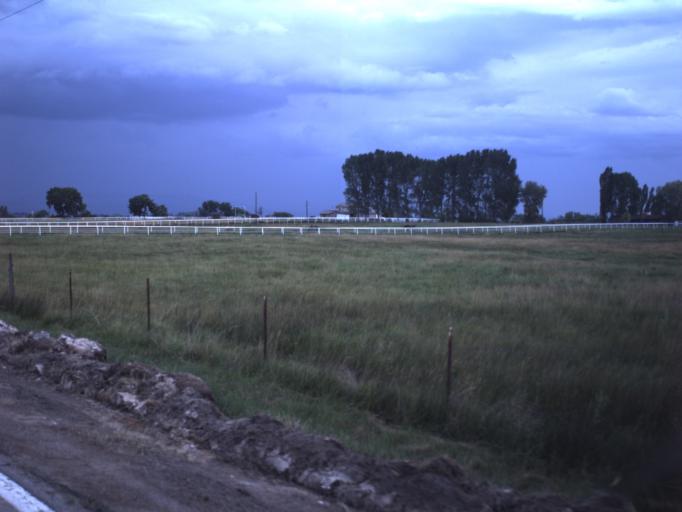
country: US
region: Utah
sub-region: Duchesne County
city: Roosevelt
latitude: 40.3609
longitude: -110.0296
